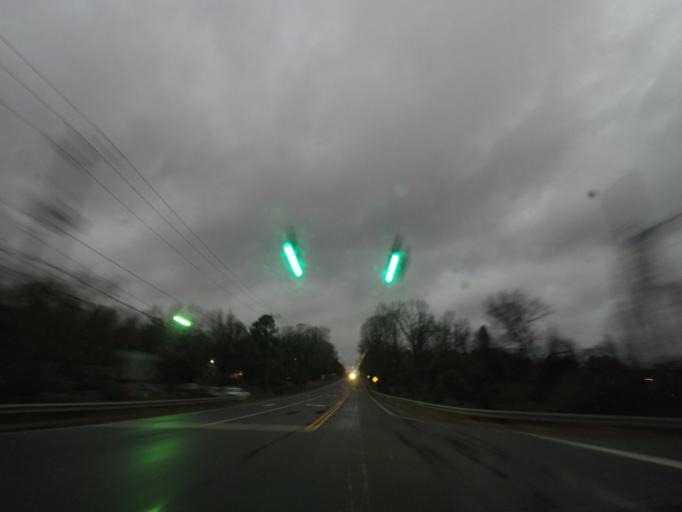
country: US
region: North Carolina
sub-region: Orange County
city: Hillsborough
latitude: 36.0921
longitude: -79.1044
